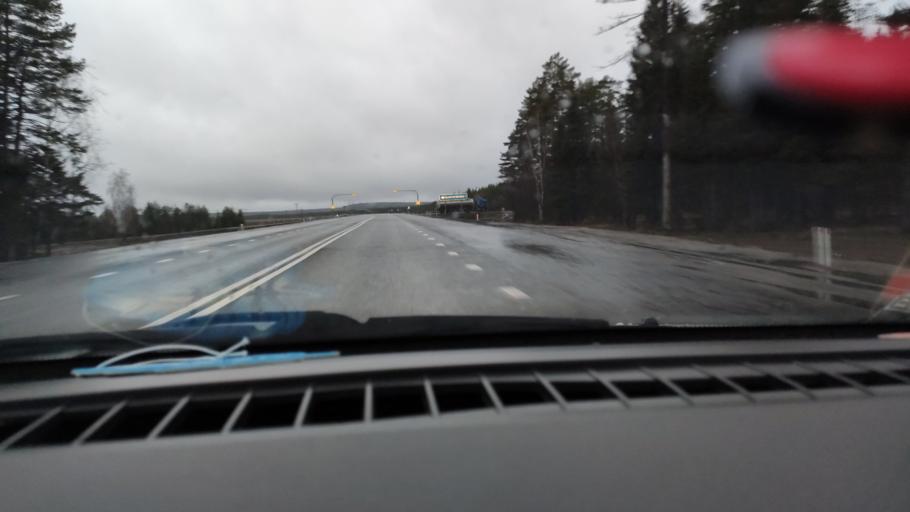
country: RU
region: Udmurtiya
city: Alnashi
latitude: 56.0846
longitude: 52.4198
